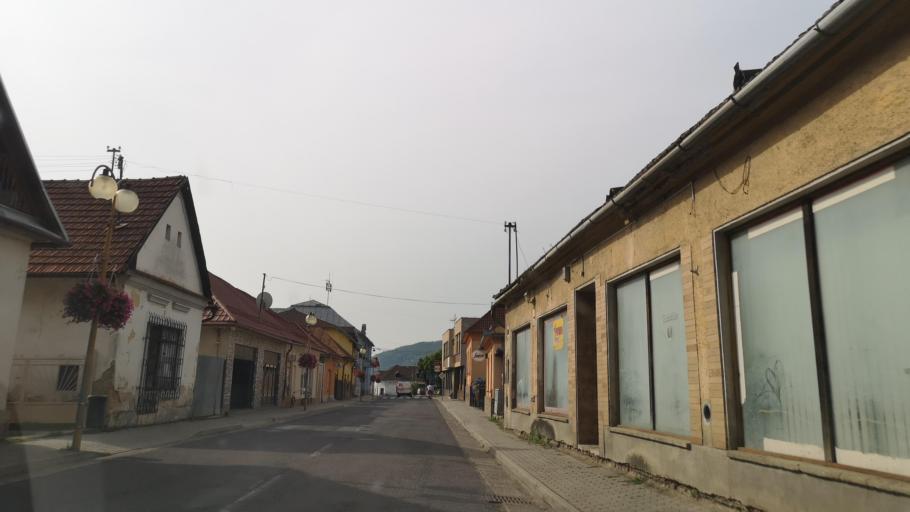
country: SK
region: Banskobystricky
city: Tisovec
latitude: 48.5723
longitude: 19.8407
